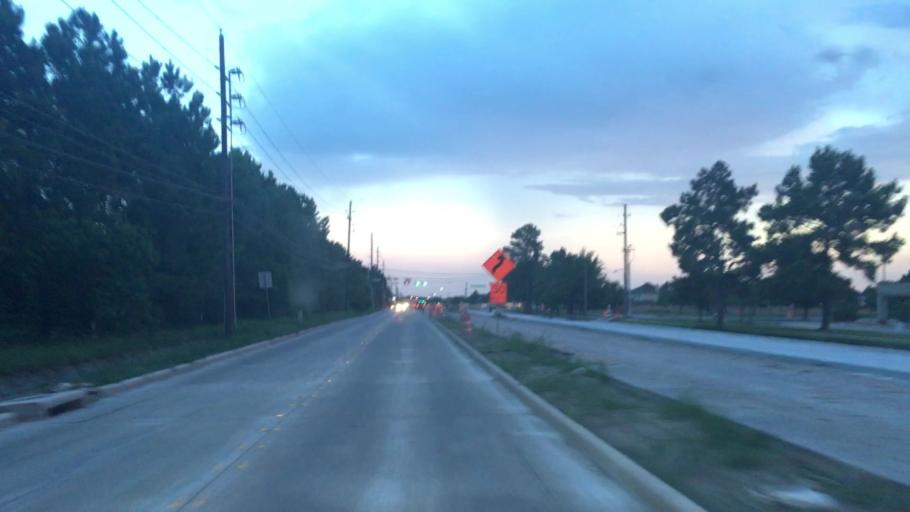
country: US
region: Texas
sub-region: Harris County
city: Humble
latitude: 29.9454
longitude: -95.2496
